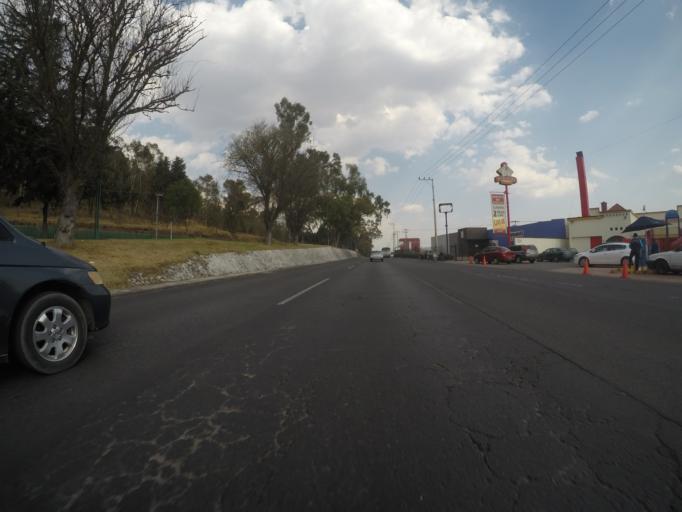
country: MX
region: Morelos
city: Metepec
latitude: 19.2464
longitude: -99.6076
